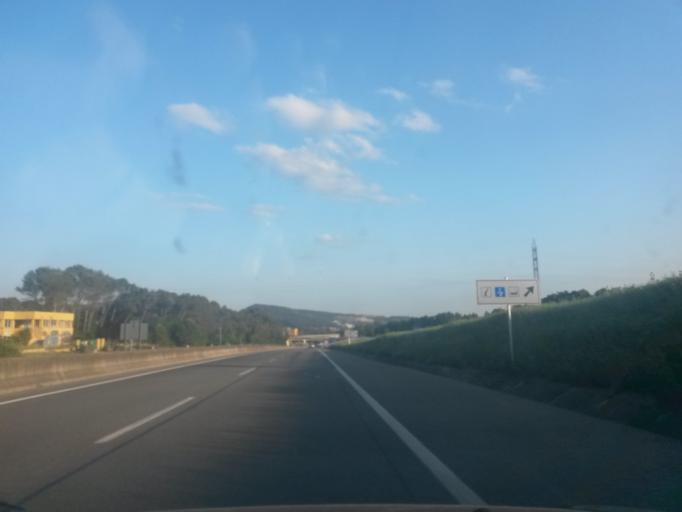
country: ES
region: Catalonia
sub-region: Provincia de Girona
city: Palol de Revardit
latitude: 42.0457
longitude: 2.8198
